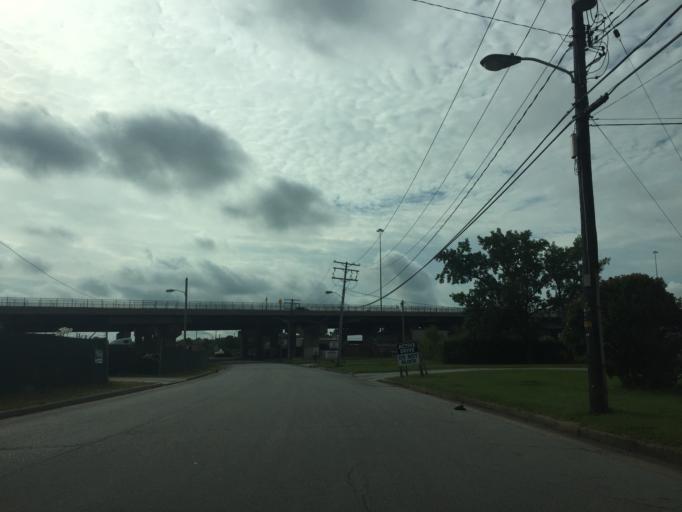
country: US
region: Maryland
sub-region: Baltimore County
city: Rosedale
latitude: 39.3020
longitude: -76.5324
